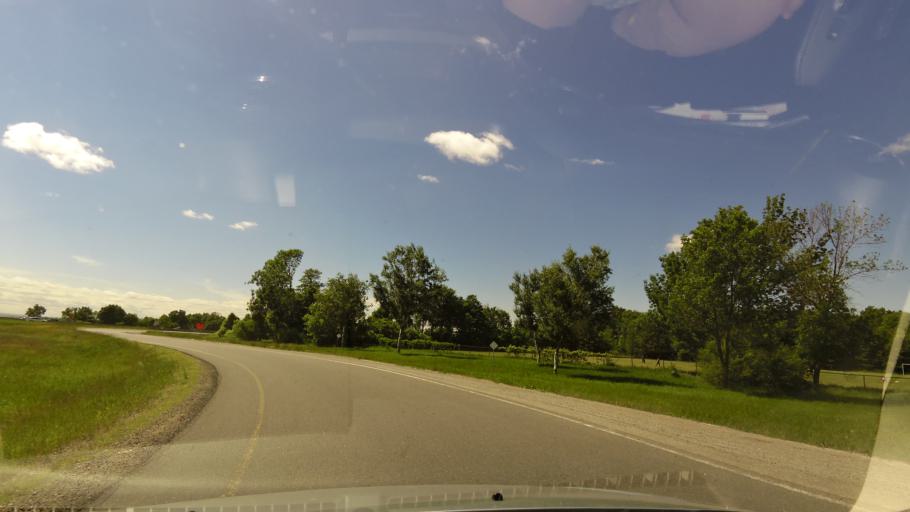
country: CA
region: Ontario
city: Bradford West Gwillimbury
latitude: 44.0028
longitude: -79.5842
